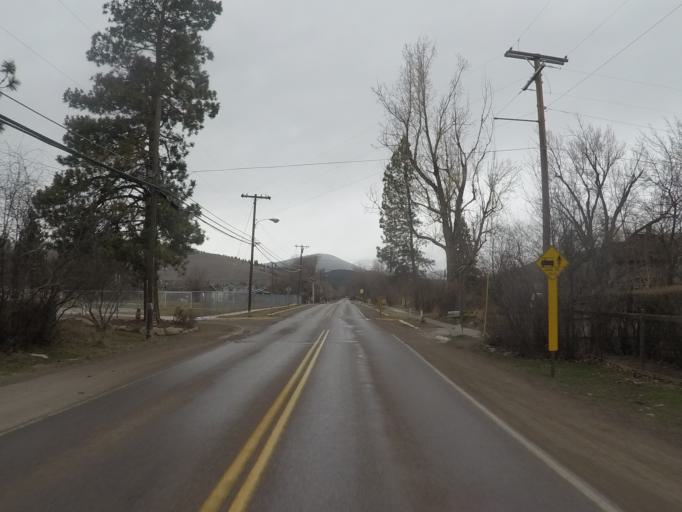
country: US
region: Montana
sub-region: Missoula County
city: East Missoula
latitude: 46.8909
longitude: -113.9656
